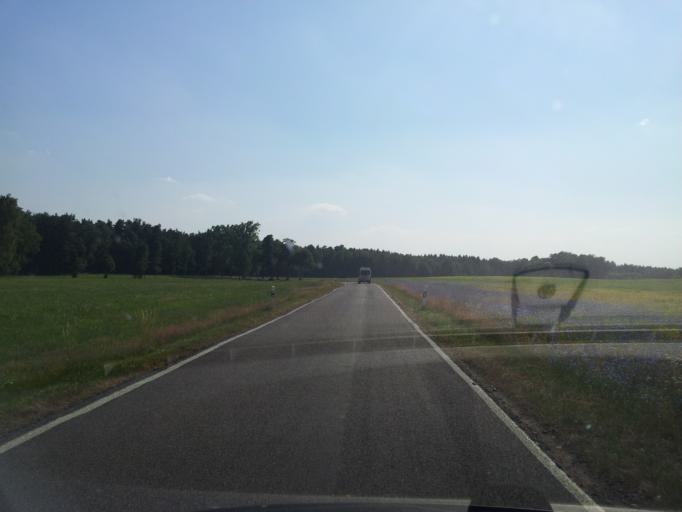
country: DE
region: Saxony
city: Hockendorf
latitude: 51.2138
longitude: 13.9056
